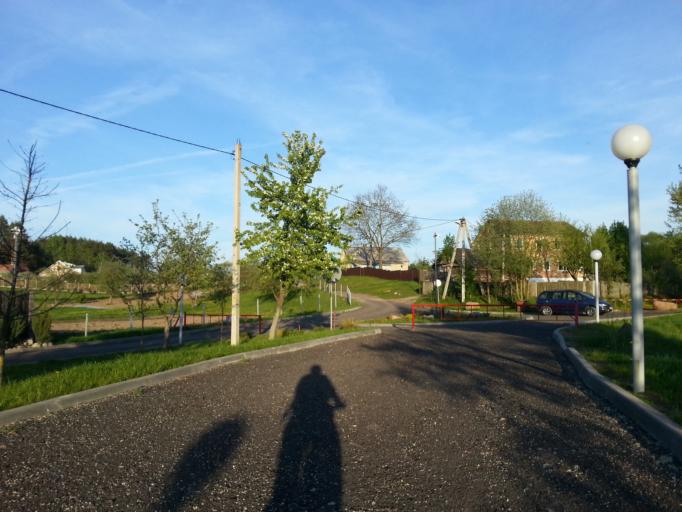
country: BY
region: Minsk
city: Slabada
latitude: 54.0506
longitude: 27.8652
